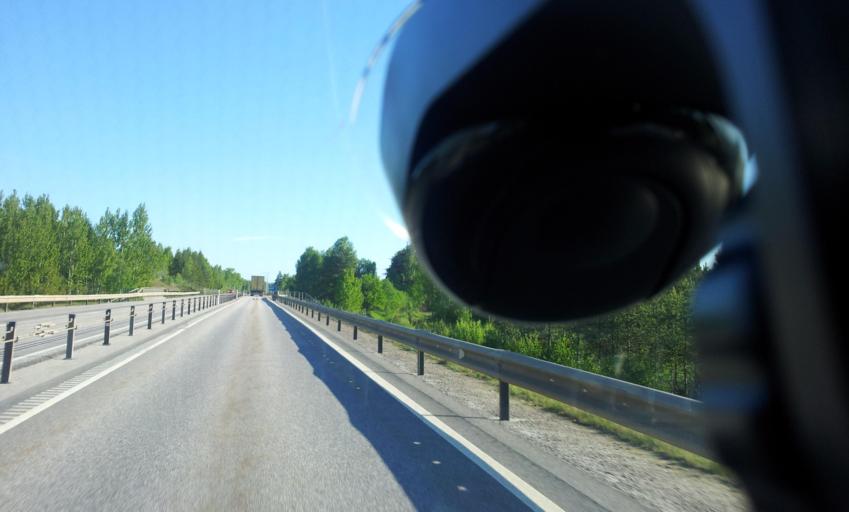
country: SE
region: Kalmar
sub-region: Vasterviks Kommun
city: Vaestervik
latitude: 57.7540
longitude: 16.5572
